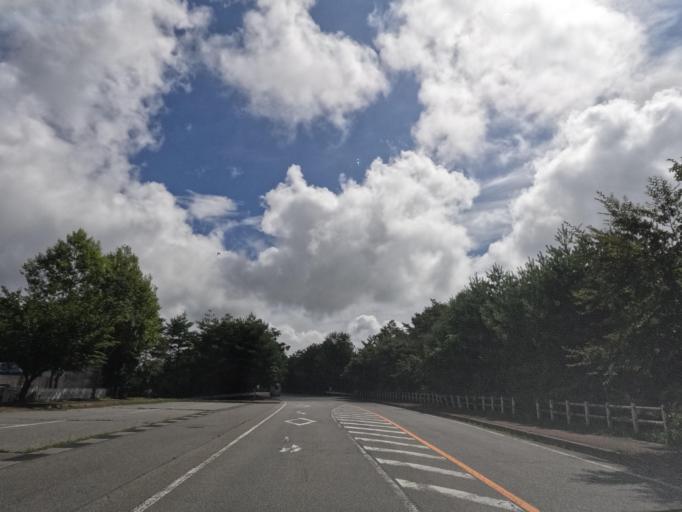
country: JP
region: Yamanashi
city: Nirasaki
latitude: 35.8874
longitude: 138.4174
